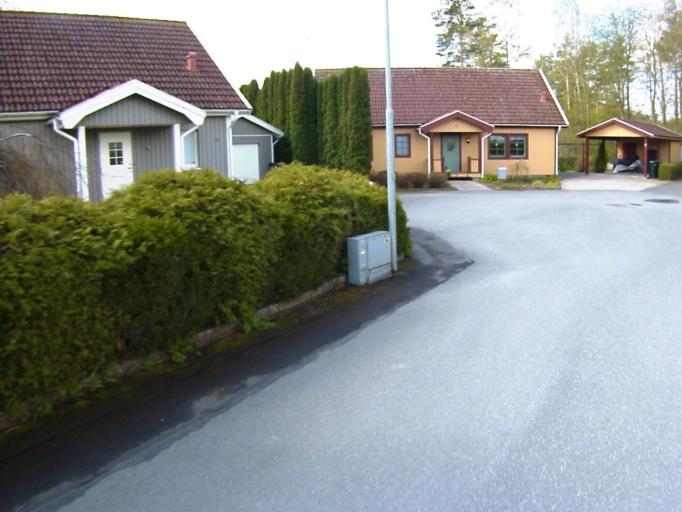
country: SE
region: Skane
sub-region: Kristianstads Kommun
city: Norra Asum
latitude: 56.0086
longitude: 14.0889
